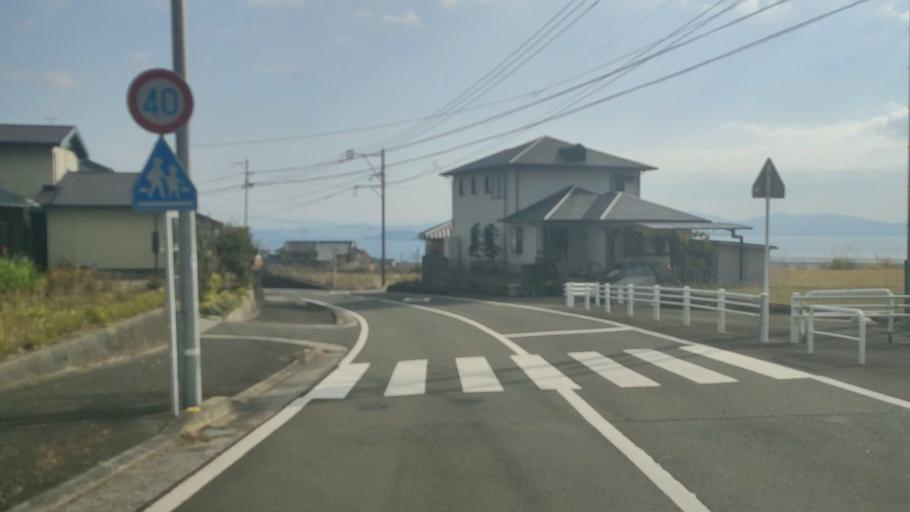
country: JP
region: Nagasaki
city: Shimabara
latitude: 32.6782
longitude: 130.2791
